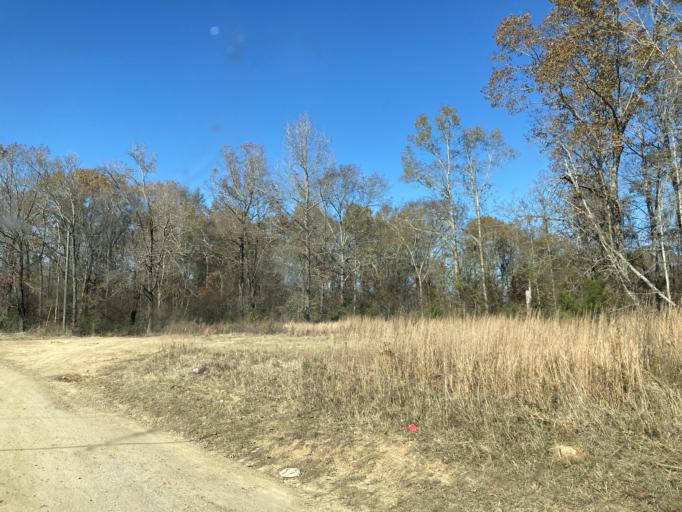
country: US
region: Mississippi
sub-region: Holmes County
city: Pickens
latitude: 32.8557
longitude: -90.0141
